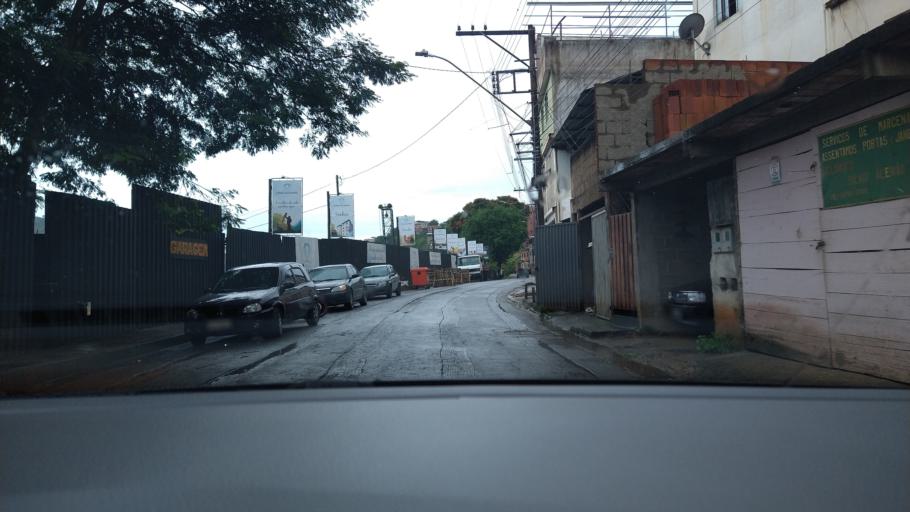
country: BR
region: Minas Gerais
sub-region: Ponte Nova
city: Ponte Nova
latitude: -20.4003
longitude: -42.9009
